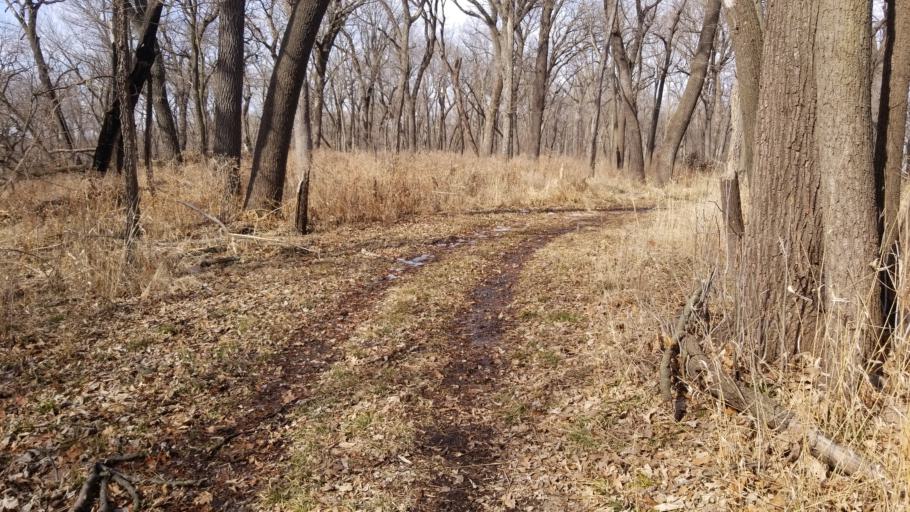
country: US
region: Nebraska
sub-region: Sarpy County
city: Bellevue
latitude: 41.1731
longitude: -95.9011
